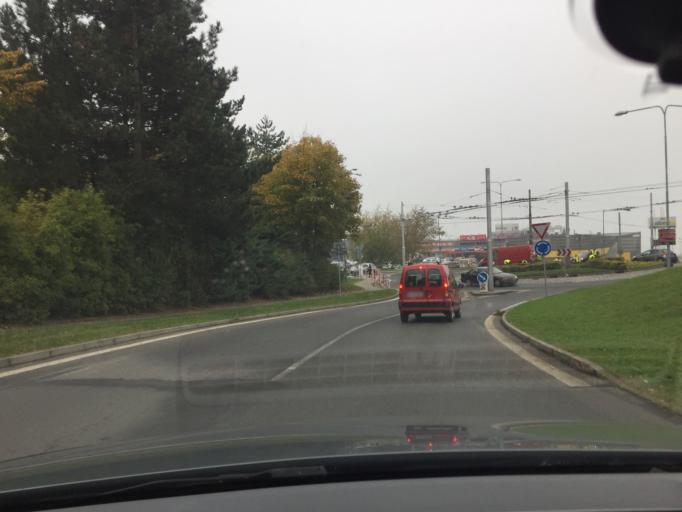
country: CZ
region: Ustecky
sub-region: Okres Usti nad Labem
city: Usti nad Labem
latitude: 50.6794
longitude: 14.0370
